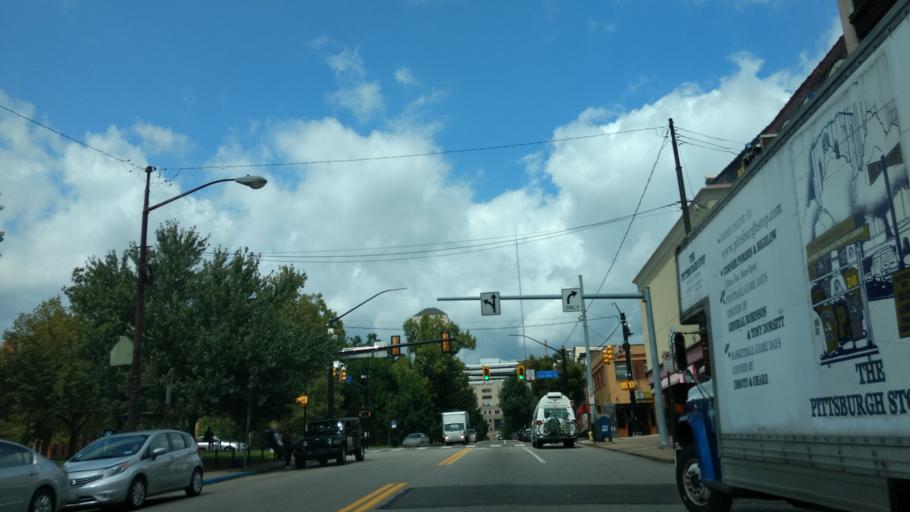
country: US
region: Pennsylvania
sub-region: Allegheny County
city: Pittsburgh
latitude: 40.4529
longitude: -80.0015
